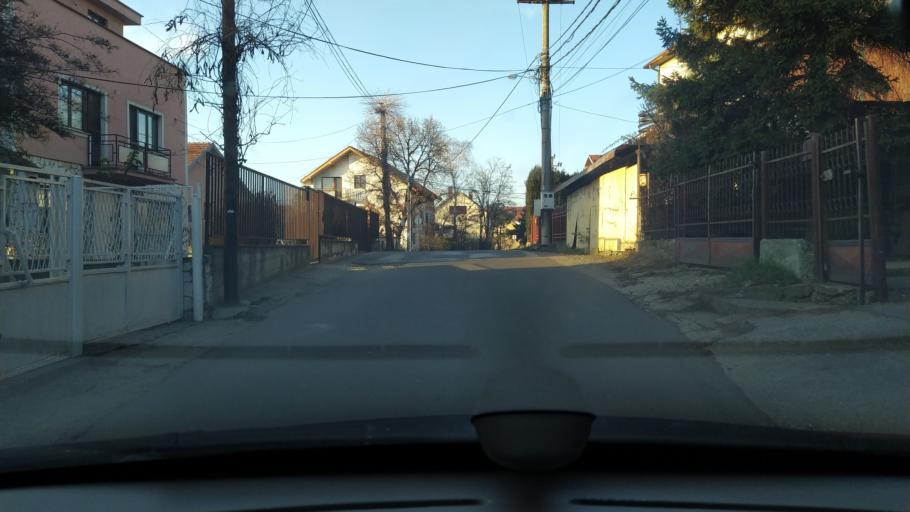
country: RS
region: Central Serbia
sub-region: Belgrade
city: Zvezdara
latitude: 44.7597
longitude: 20.5648
